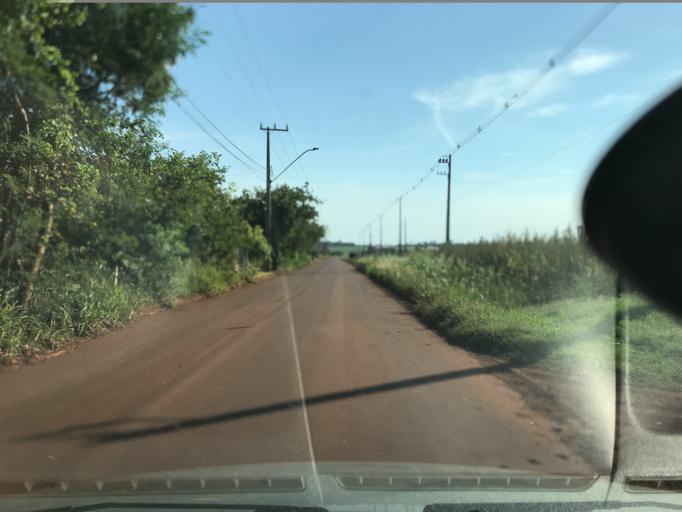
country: BR
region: Parana
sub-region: Palotina
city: Palotina
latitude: -24.2919
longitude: -53.8275
